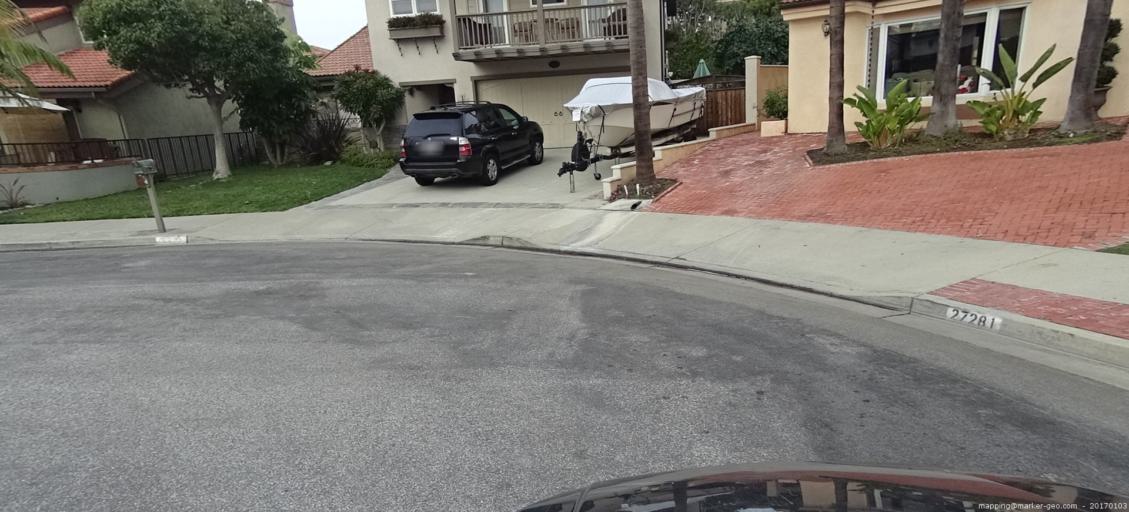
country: US
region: California
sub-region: Orange County
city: Dana Point
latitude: 33.4513
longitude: -117.6548
